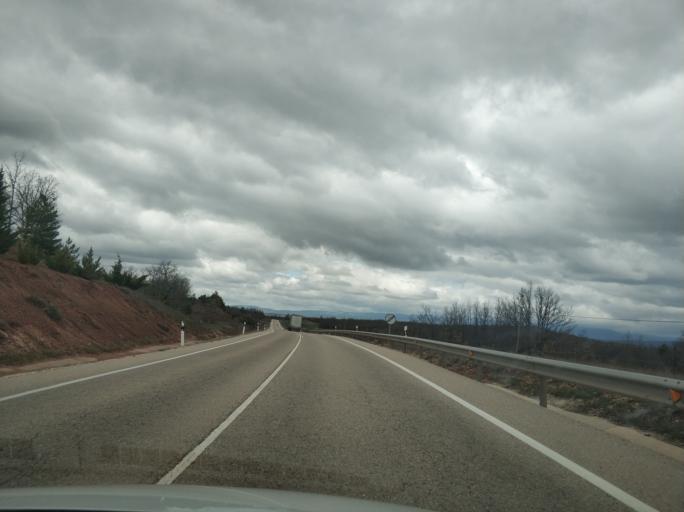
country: ES
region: Castille and Leon
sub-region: Provincia de Burgos
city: Hacinas
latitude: 41.9616
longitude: -3.2916
